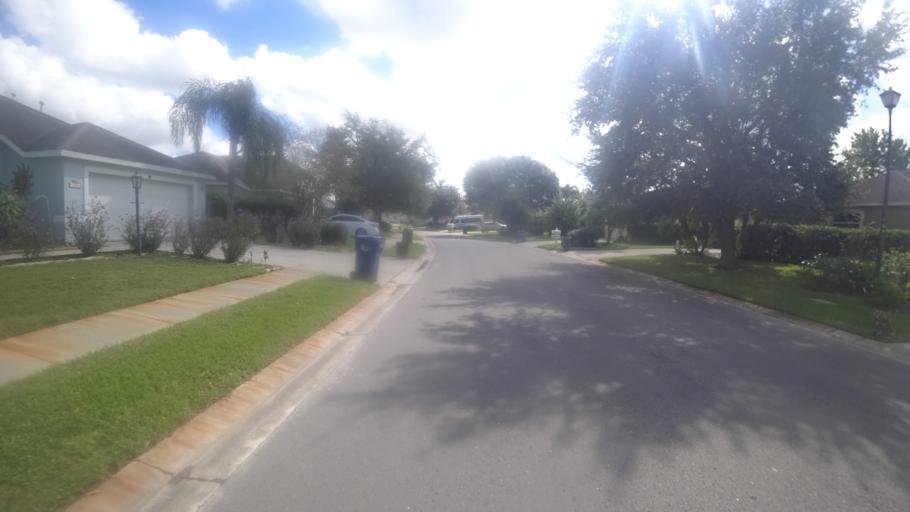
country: US
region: Florida
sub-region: Manatee County
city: Ellenton
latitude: 27.4936
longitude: -82.4397
